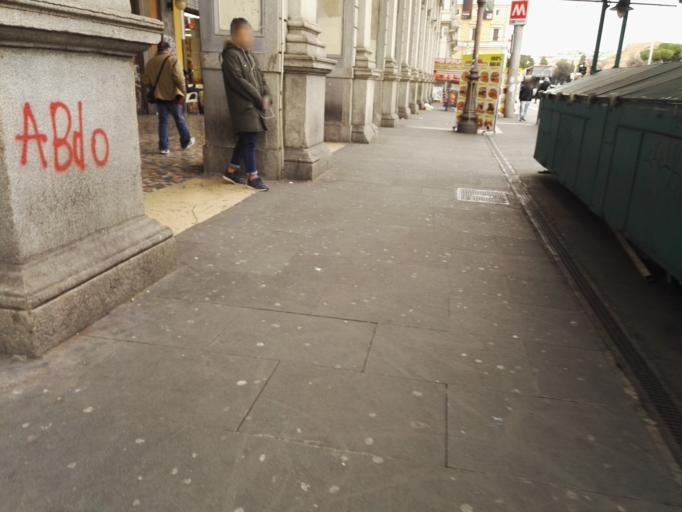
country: IT
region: Latium
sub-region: Citta metropolitana di Roma Capitale
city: Rome
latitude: 41.9004
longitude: 12.5003
